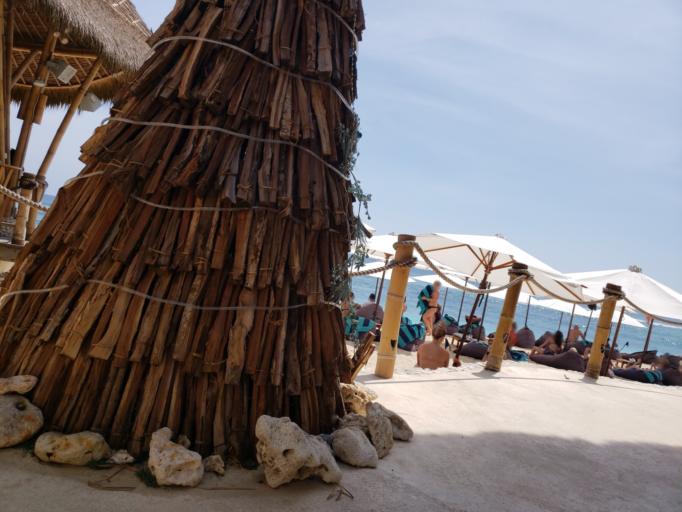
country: ID
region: Bali
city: Kangin
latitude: -8.8472
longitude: 115.1508
